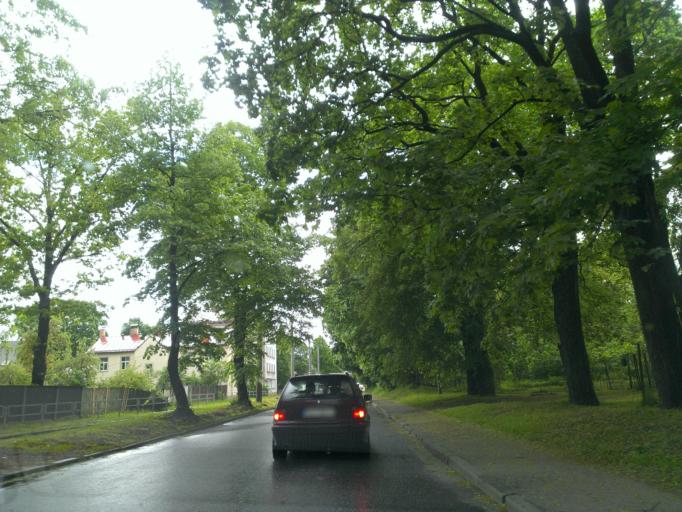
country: LV
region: Riga
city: Riga
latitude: 56.9185
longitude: 24.1019
